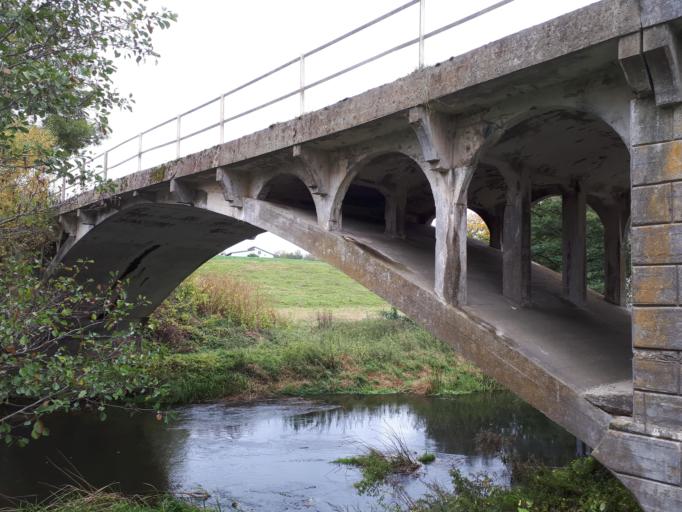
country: LT
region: Marijampoles apskritis
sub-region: Marijampole Municipality
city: Marijampole
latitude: 54.4472
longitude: 23.4038
